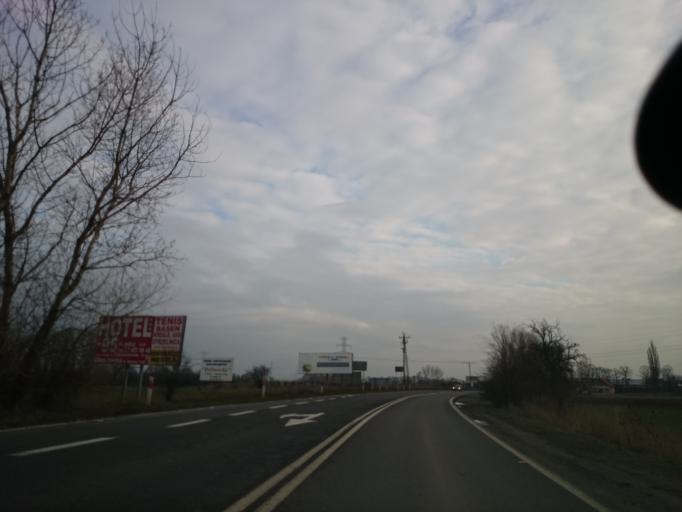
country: PL
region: Opole Voivodeship
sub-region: Powiat opolski
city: Opole
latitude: 50.6506
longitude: 17.9101
